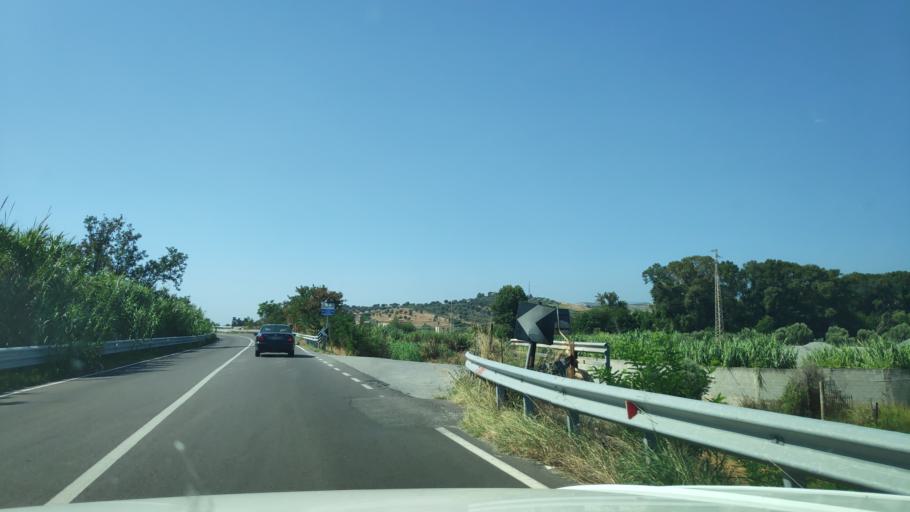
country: IT
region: Calabria
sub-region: Provincia di Reggio Calabria
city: Bovalino
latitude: 38.1297
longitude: 16.1598
